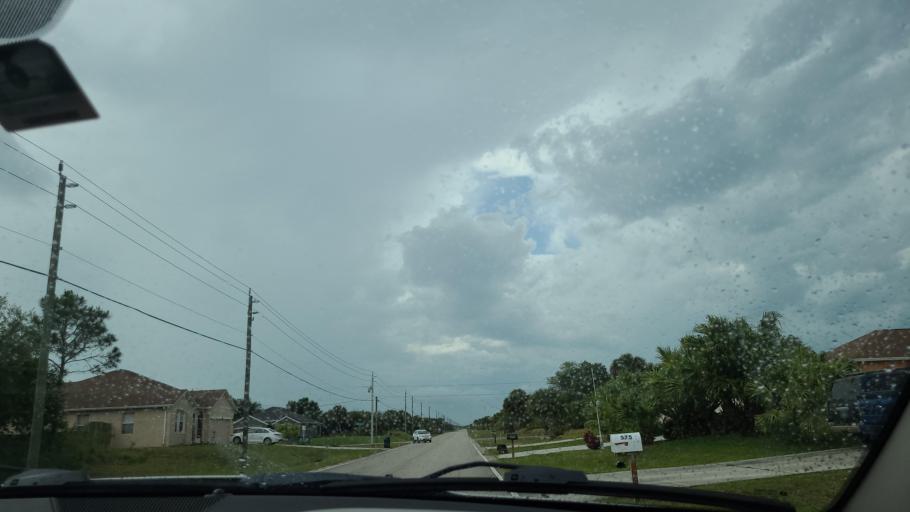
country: US
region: Florida
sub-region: Brevard County
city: Grant-Valkaria
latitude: 27.9529
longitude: -80.6866
